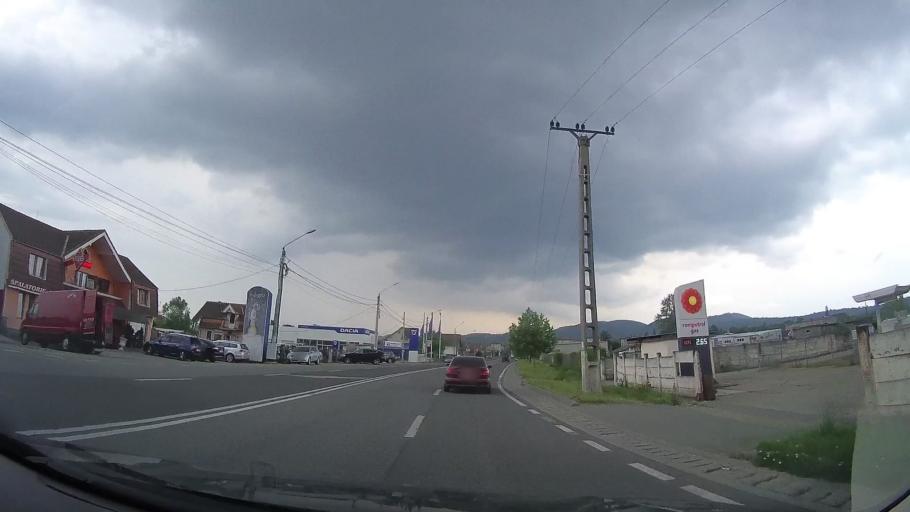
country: RO
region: Caras-Severin
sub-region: Municipiul Caransebes
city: Caransebes
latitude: 45.4265
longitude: 22.1967
